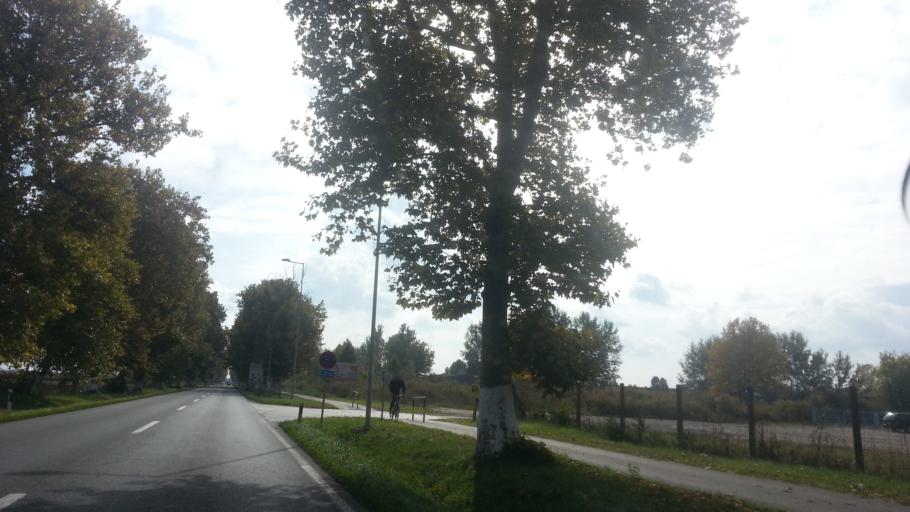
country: RS
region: Autonomna Pokrajina Vojvodina
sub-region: Sremski Okrug
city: Stara Pazova
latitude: 44.9717
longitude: 20.1756
